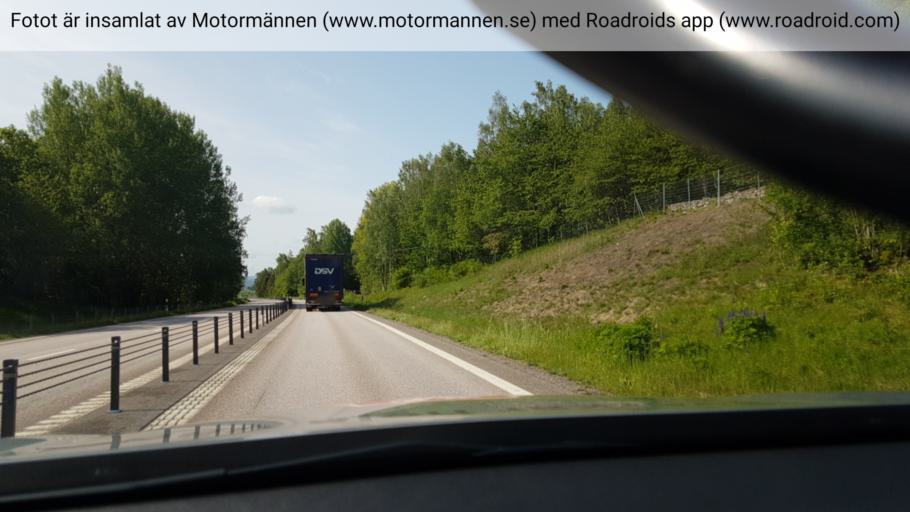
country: SE
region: Vaestra Goetaland
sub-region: Mariestads Kommun
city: Mariestad
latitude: 58.5984
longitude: 13.8016
